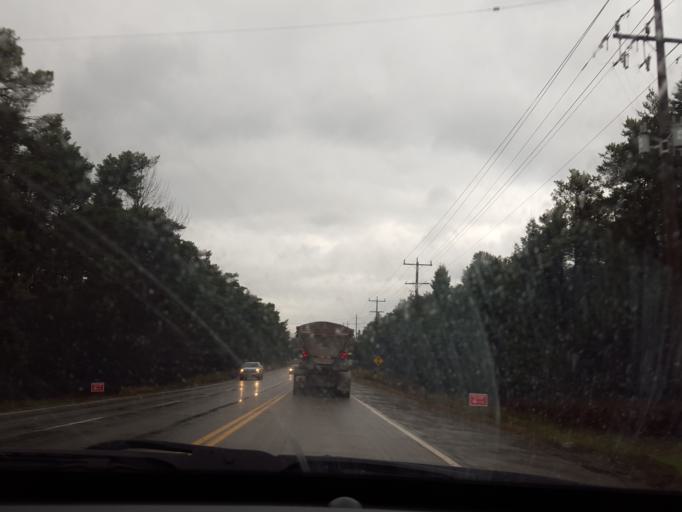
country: CA
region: Ontario
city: Uxbridge
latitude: 44.0430
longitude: -79.1462
